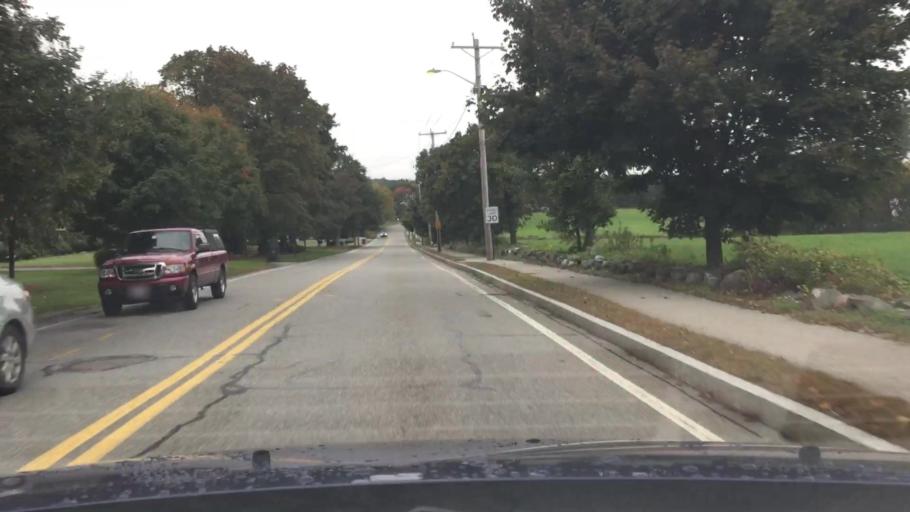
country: US
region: Massachusetts
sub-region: Middlesex County
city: Dracut
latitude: 42.6680
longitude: -71.3499
